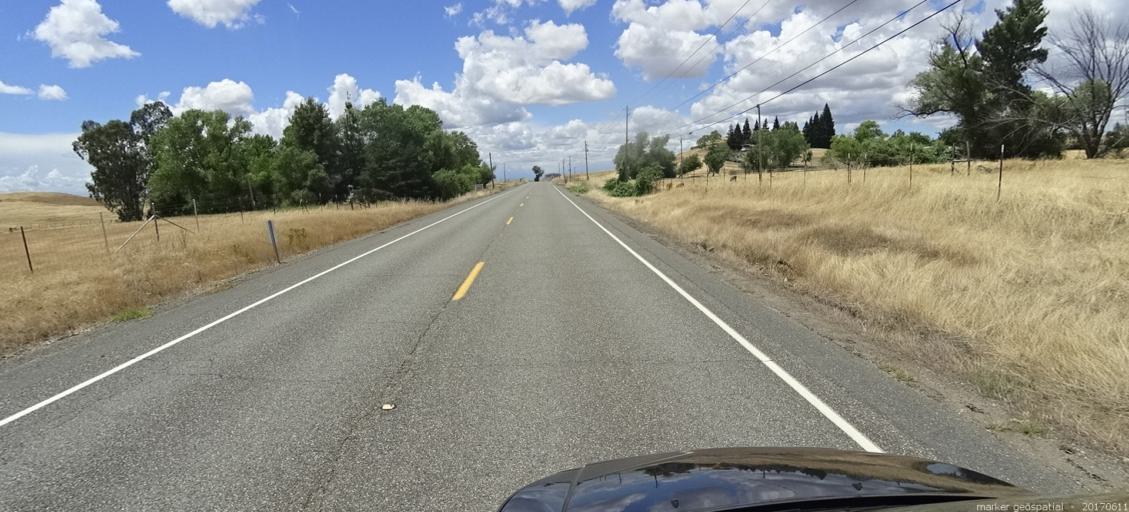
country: US
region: California
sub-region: Butte County
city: Paradise
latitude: 39.6470
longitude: -121.6137
